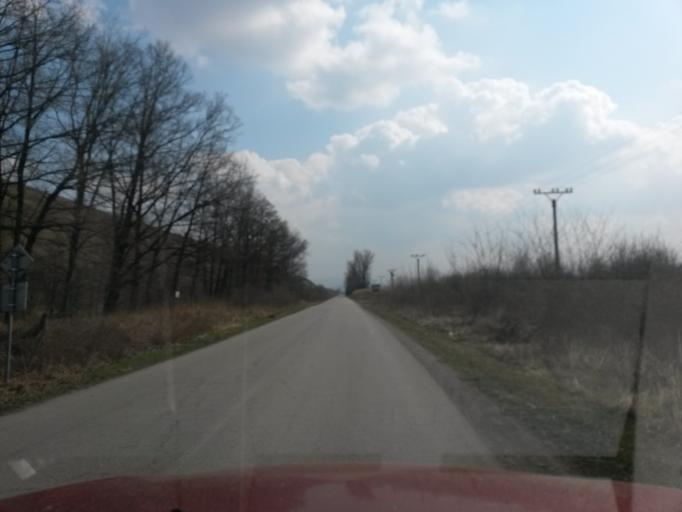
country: SK
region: Kosicky
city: Kosice
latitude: 48.5889
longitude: 21.1745
